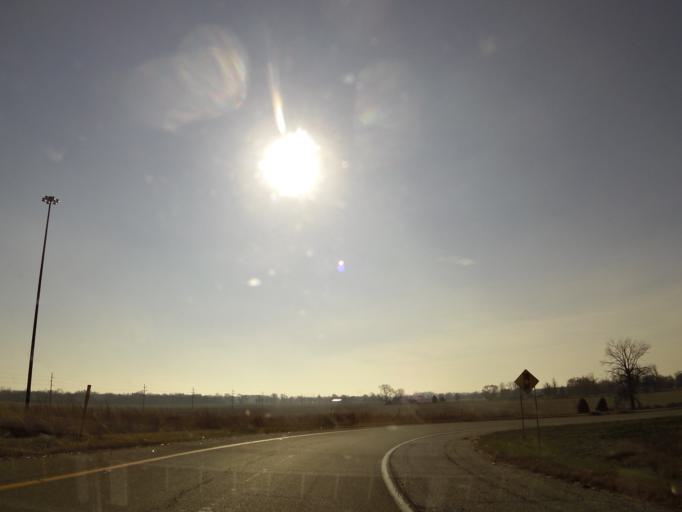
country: US
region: Indiana
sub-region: Shelby County
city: Shelbyville
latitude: 39.5252
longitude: -85.7349
